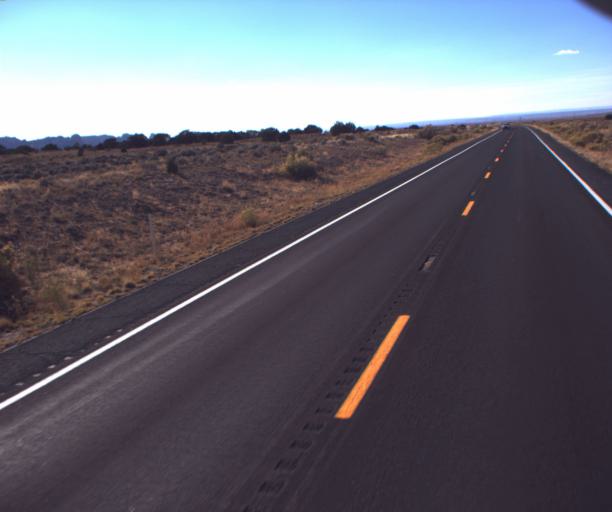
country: US
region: Arizona
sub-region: Coconino County
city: Kaibito
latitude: 36.6151
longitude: -110.9326
